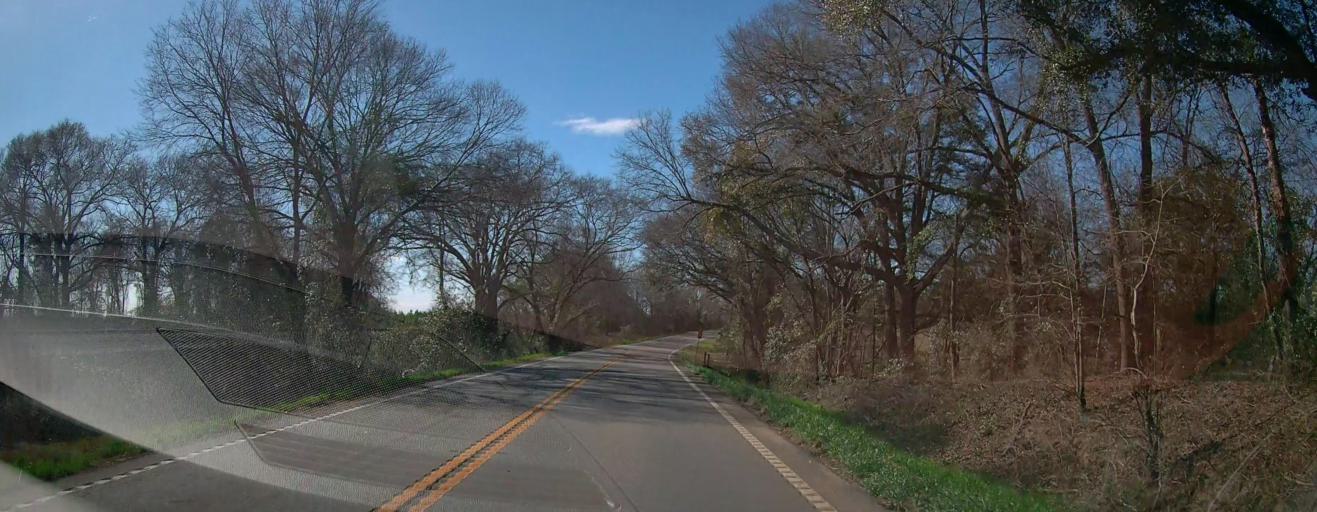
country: US
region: Georgia
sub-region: Macon County
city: Oglethorpe
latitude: 32.3370
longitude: -84.1257
